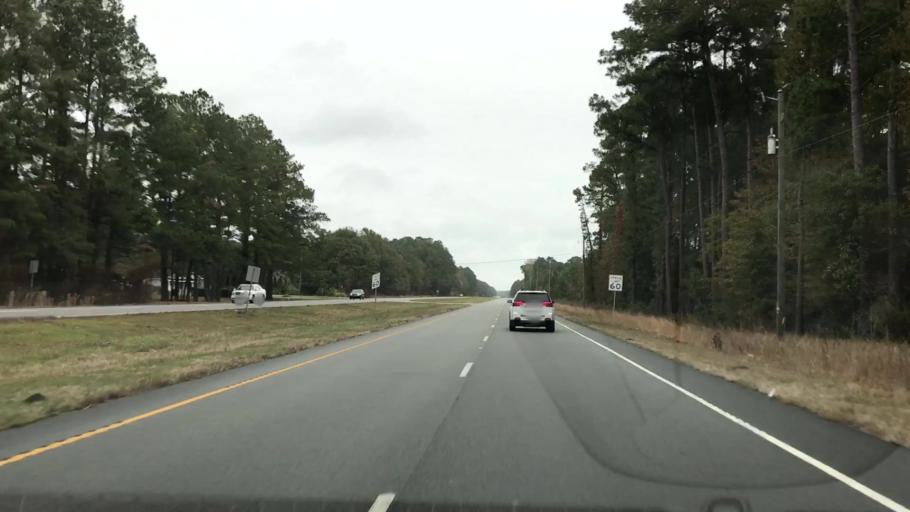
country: US
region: South Carolina
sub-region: Charleston County
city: Awendaw
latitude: 33.1036
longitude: -79.4655
